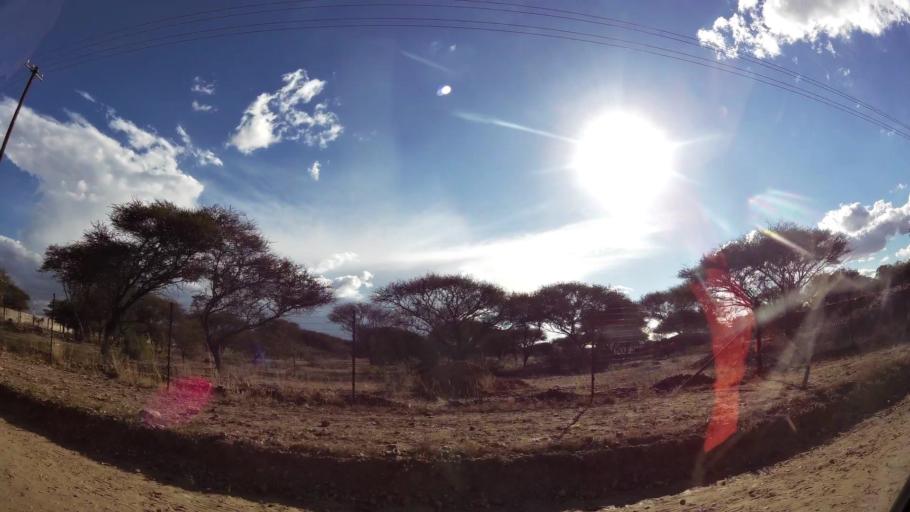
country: ZA
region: Limpopo
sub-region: Capricorn District Municipality
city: Polokwane
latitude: -23.9337
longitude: 29.4447
